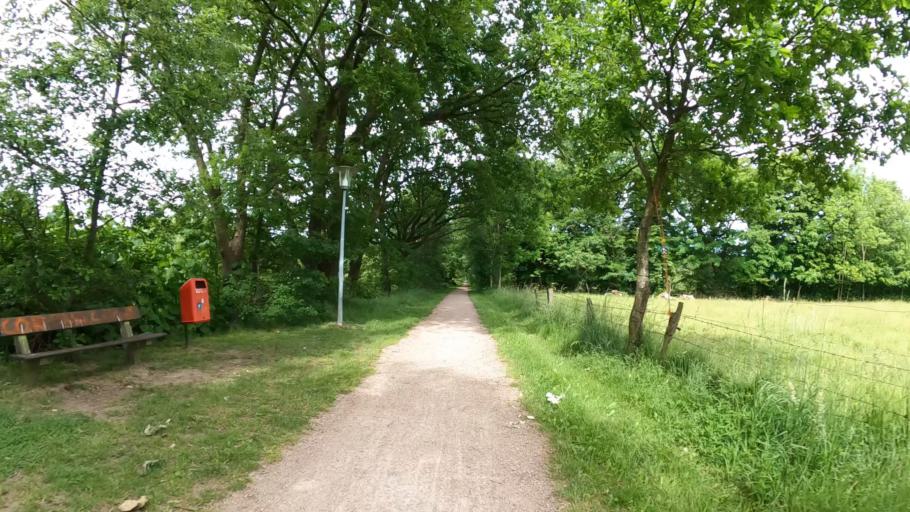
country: DE
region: Schleswig-Holstein
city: Huttblek
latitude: 53.7851
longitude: 10.0813
